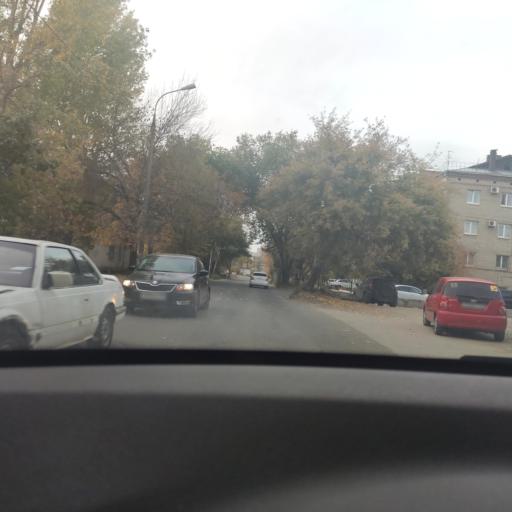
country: RU
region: Samara
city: Samara
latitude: 53.2169
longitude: 50.1983
